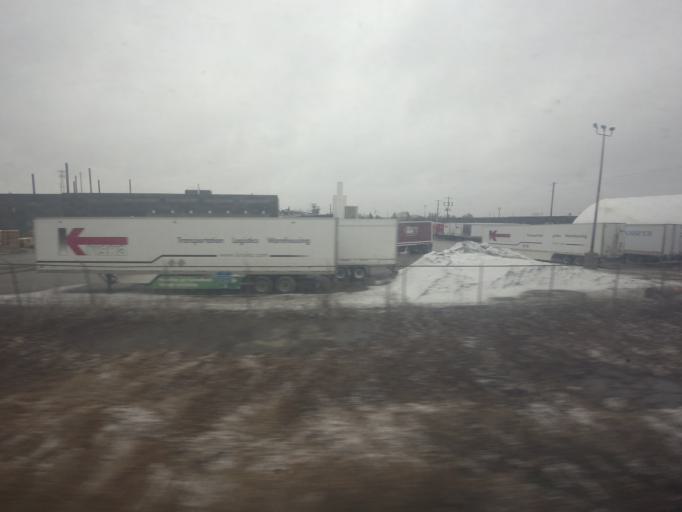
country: CA
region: Ontario
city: Brockville
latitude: 44.6117
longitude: -75.6962
